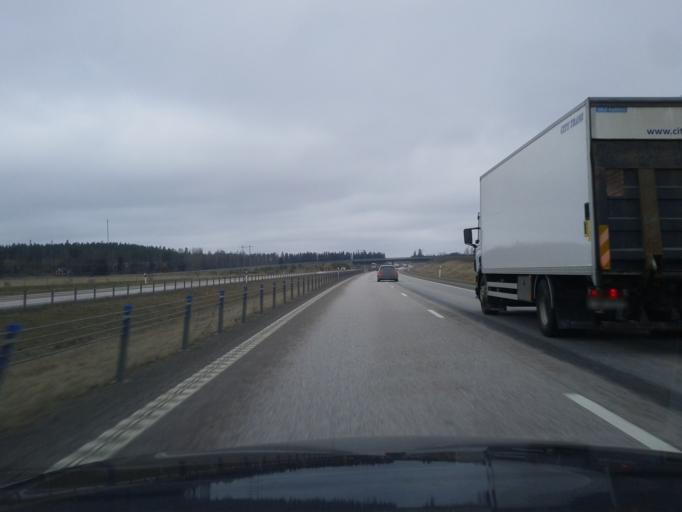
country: SE
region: Uppsala
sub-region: Osthammars Kommun
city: Bjorklinge
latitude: 60.0984
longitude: 17.5671
